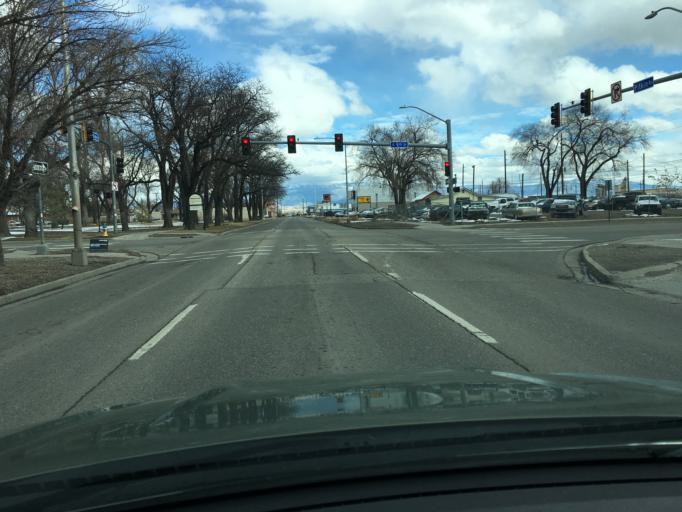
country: US
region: Colorado
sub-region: Mesa County
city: Grand Junction
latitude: 39.0644
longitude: -108.5581
